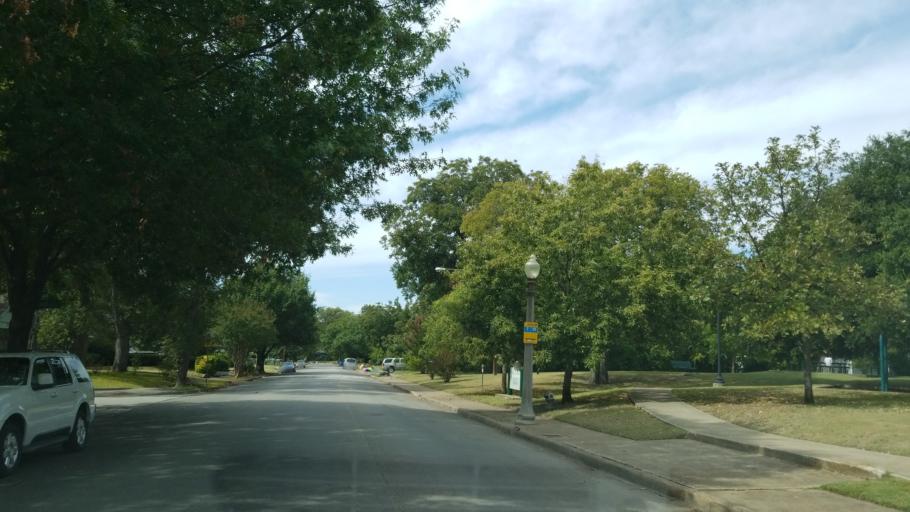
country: US
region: Texas
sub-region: Dallas County
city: Dallas
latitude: 32.7894
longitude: -96.7403
